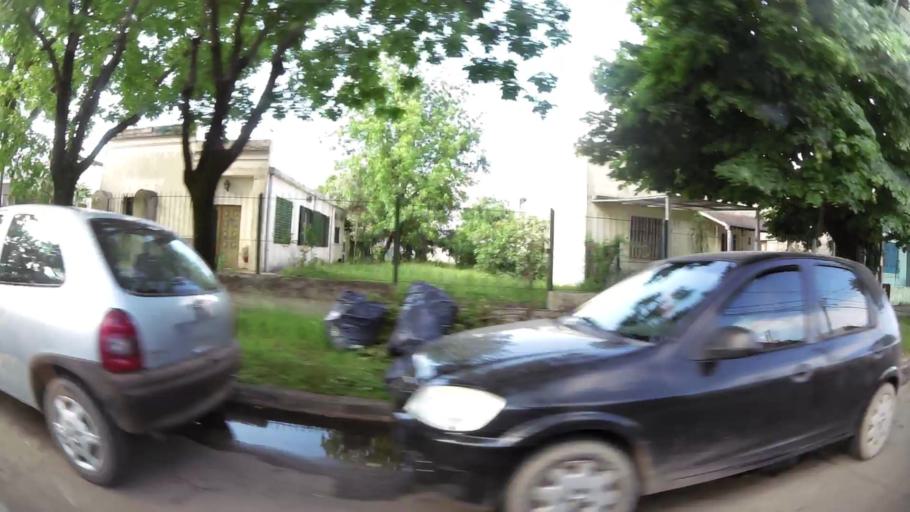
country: AR
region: Buenos Aires
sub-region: Partido de Merlo
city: Merlo
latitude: -34.6613
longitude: -58.7292
